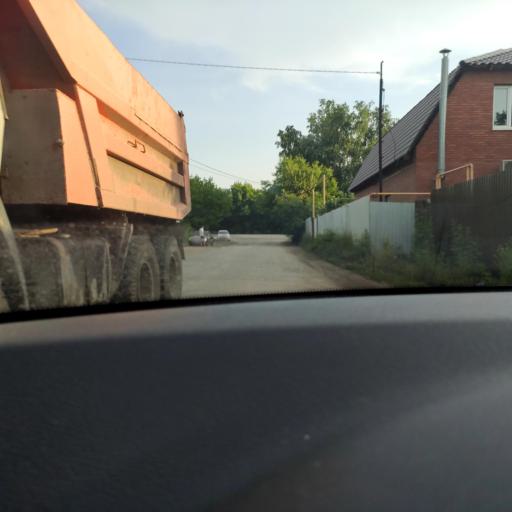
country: RU
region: Samara
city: Rozhdestveno
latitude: 53.1462
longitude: 50.0287
